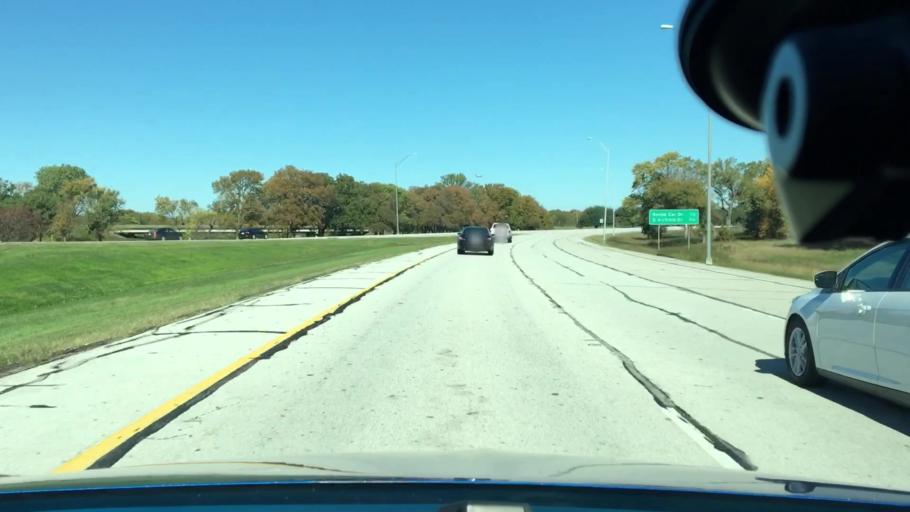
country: US
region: Texas
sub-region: Tarrant County
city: Euless
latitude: 32.8406
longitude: -97.0387
